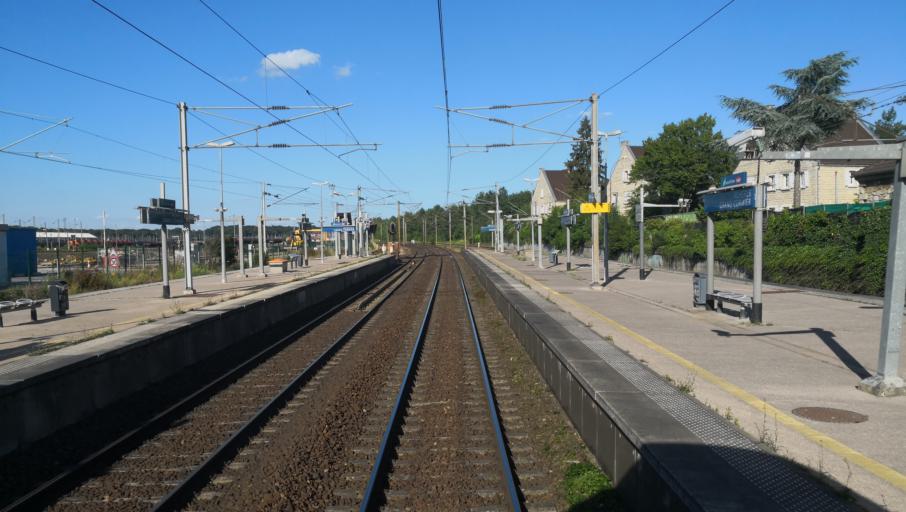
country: FR
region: Ile-de-France
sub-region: Departement des Yvelines
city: Acheres
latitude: 48.9555
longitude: 2.0944
